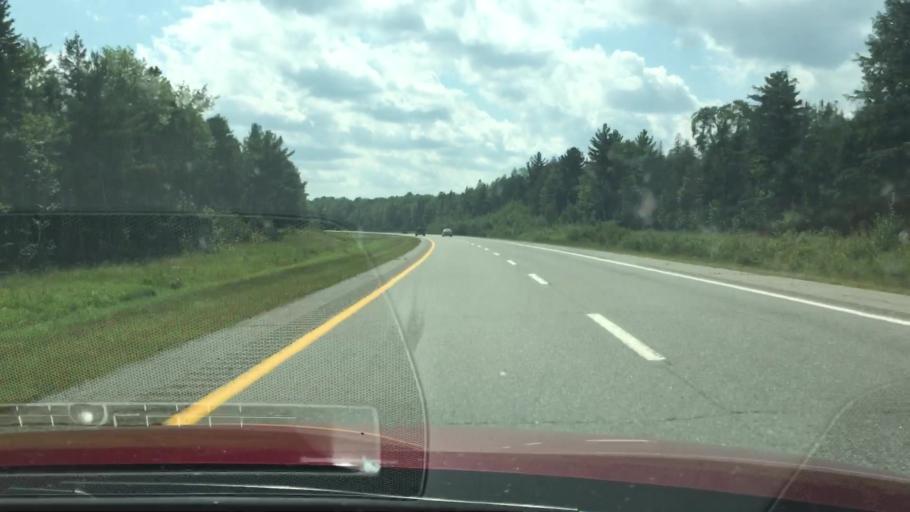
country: US
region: Maine
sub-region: Penobscot County
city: Howland
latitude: 45.3164
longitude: -68.6556
